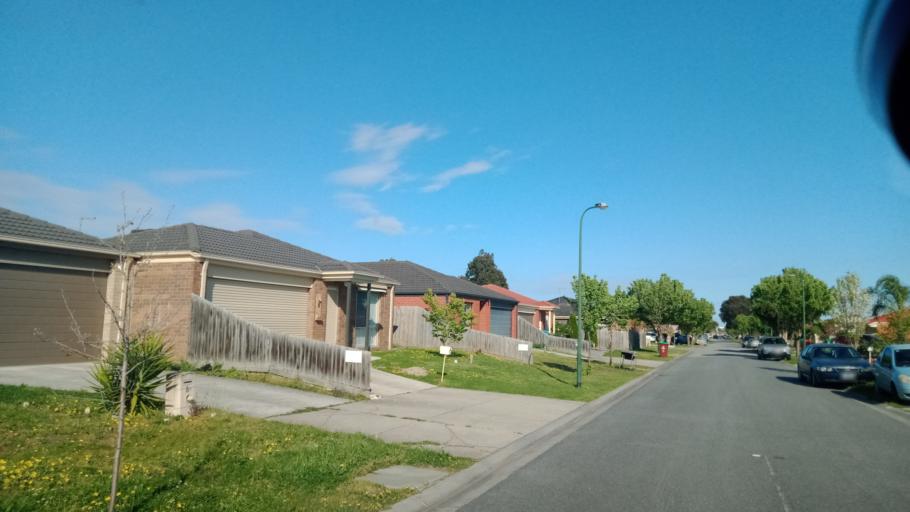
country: AU
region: Victoria
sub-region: Casey
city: Cranbourne West
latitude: -38.0932
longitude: 145.2616
